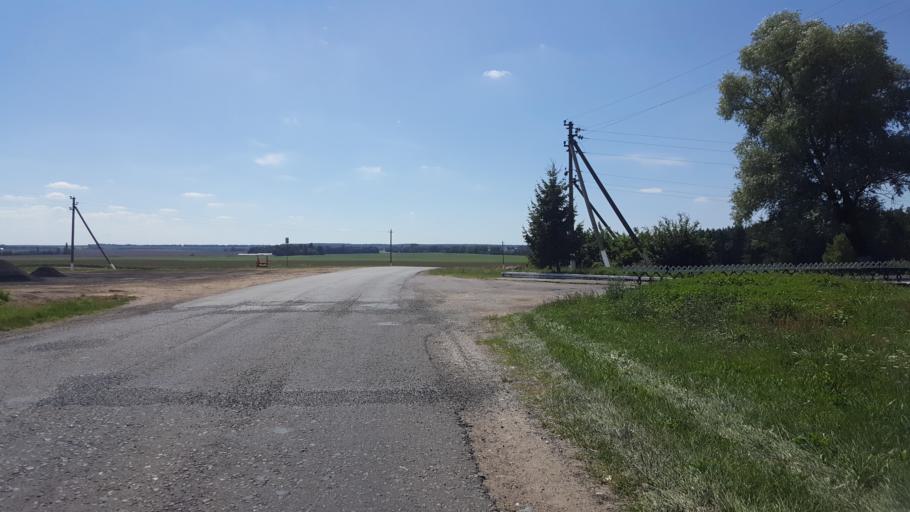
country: BY
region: Brest
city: Charnawchytsy
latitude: 52.2793
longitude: 23.6024
